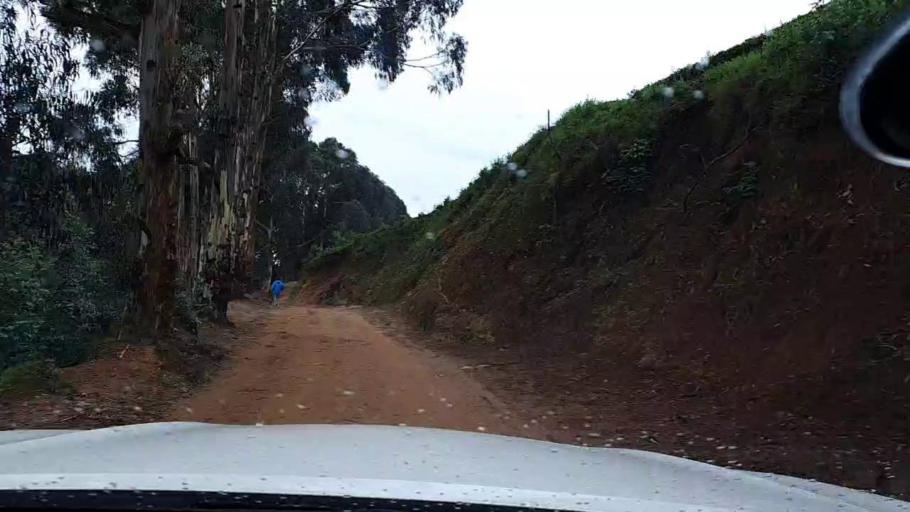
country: RW
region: Southern Province
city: Nzega
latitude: -2.3783
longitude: 29.2438
